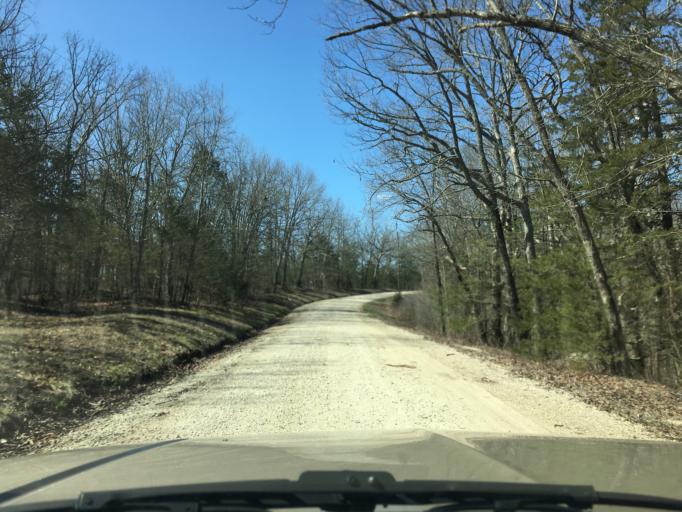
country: US
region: Missouri
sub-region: Franklin County
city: Gerald
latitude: 38.5212
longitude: -91.3171
